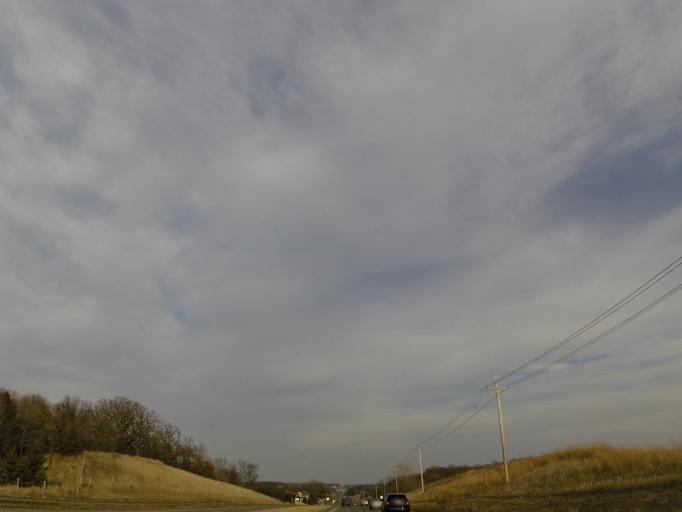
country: US
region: Minnesota
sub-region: Dakota County
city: Lakeville
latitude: 44.6813
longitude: -93.3221
